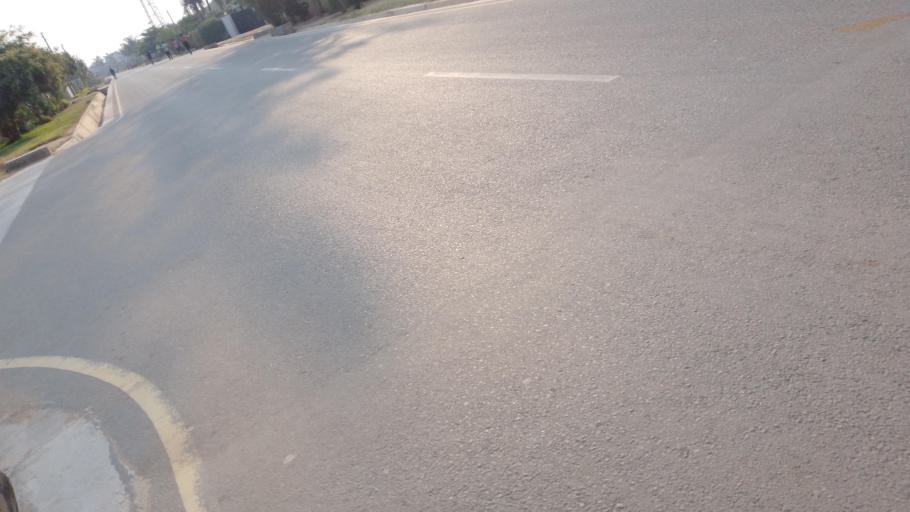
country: ZM
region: Lusaka
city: Lusaka
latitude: -15.3991
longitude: 28.3873
